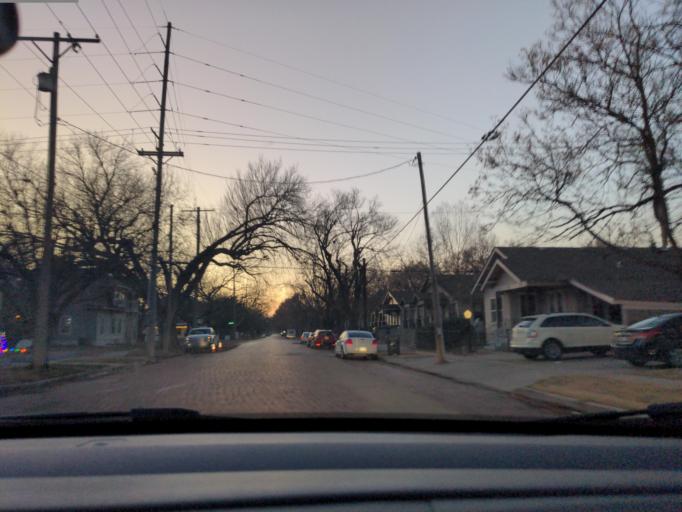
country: US
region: Kansas
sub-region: Sedgwick County
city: Wichita
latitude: 37.7044
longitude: -97.3486
